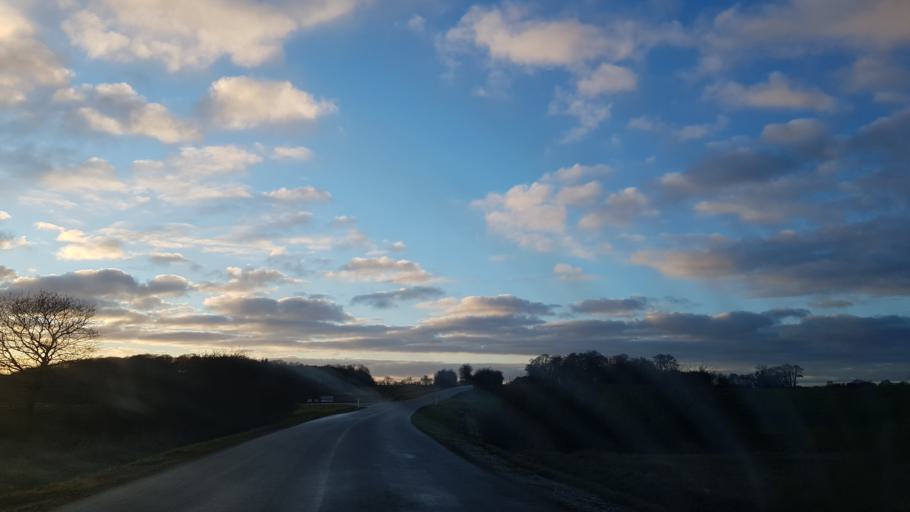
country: DK
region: South Denmark
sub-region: Kolding Kommune
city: Vamdrup
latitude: 55.3630
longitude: 9.3340
